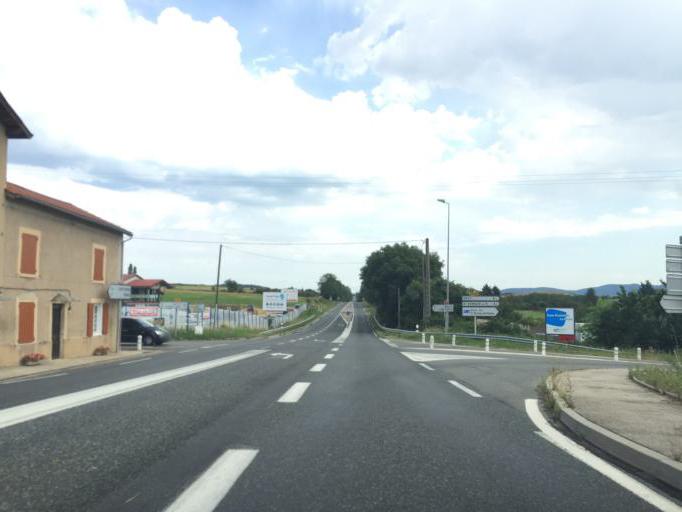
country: FR
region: Rhone-Alpes
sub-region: Departement du Rhone
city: Saint-Romain-de-Popey
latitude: 45.8672
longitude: 4.5458
